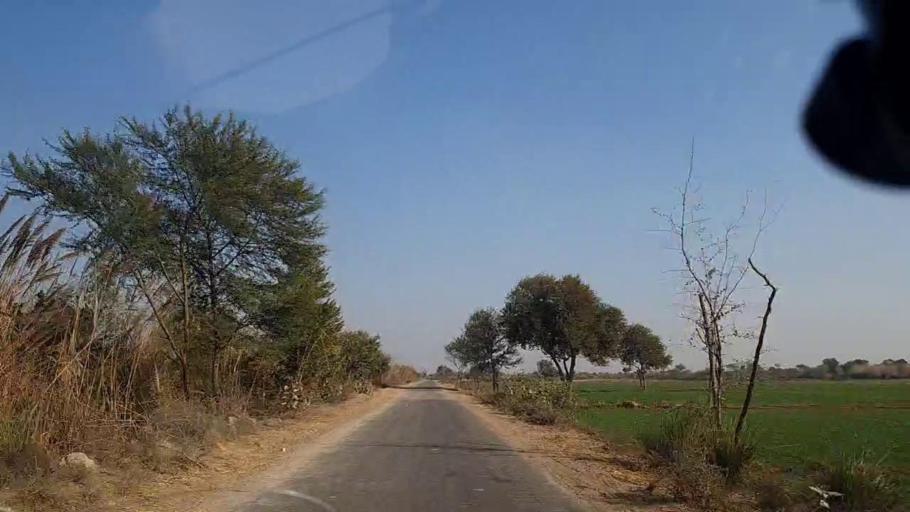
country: PK
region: Sindh
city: Khanpur
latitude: 27.6862
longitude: 69.5212
